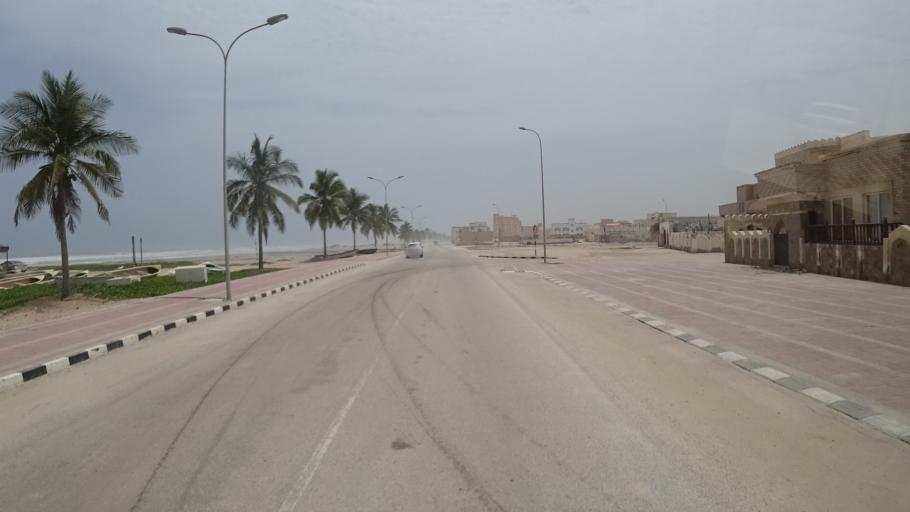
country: OM
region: Zufar
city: Salalah
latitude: 17.0348
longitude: 54.4045
